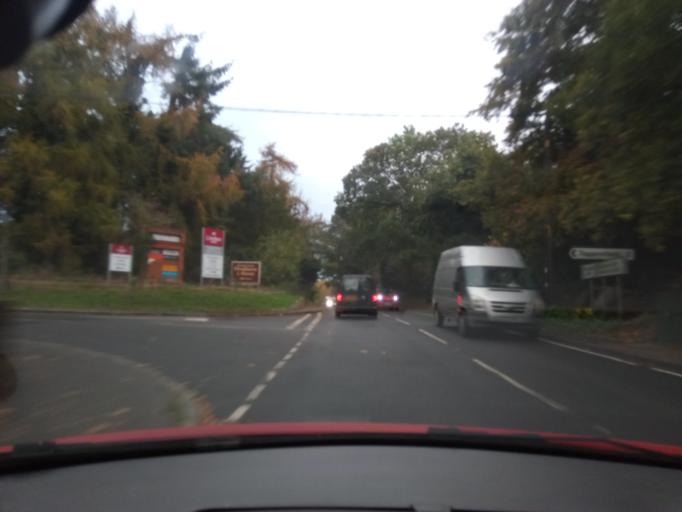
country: GB
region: England
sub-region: Essex
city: Great Yeldham
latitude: 52.0116
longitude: 0.5656
